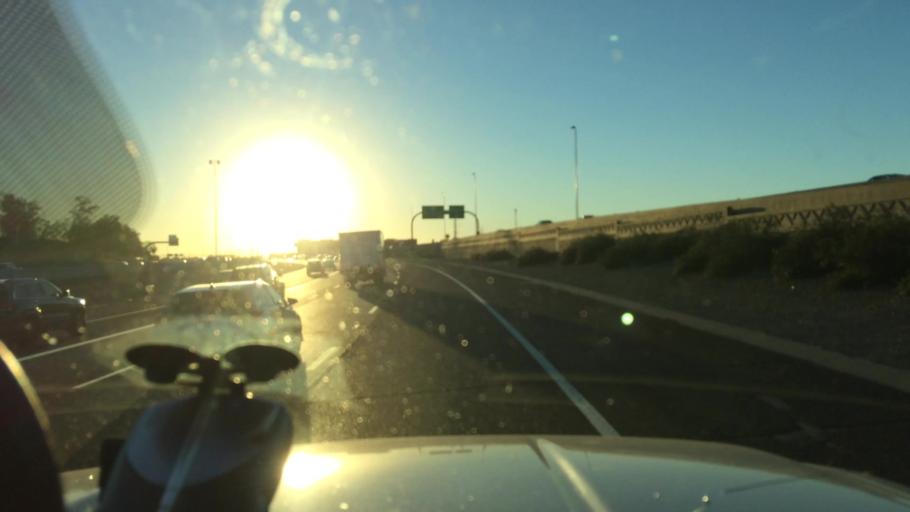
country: US
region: Arizona
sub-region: Maricopa County
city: Sun City
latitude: 33.6681
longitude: -112.2229
